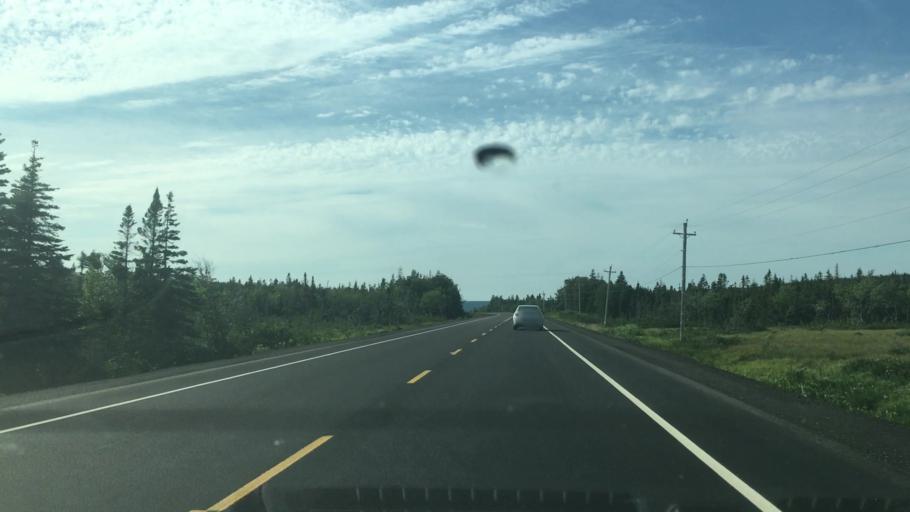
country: CA
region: Nova Scotia
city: Sydney Mines
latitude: 46.8474
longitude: -60.4138
